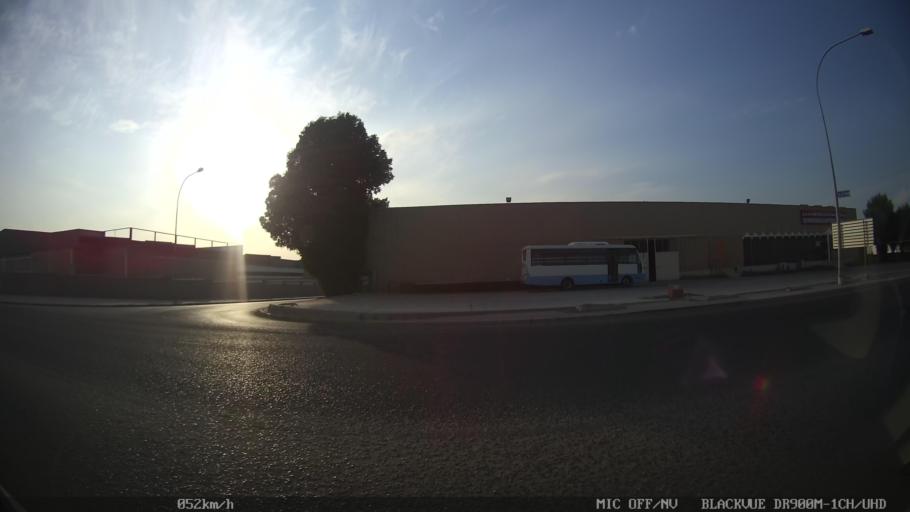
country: KW
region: Al Farwaniyah
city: Janub as Surrah
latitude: 29.2373
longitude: 48.0095
